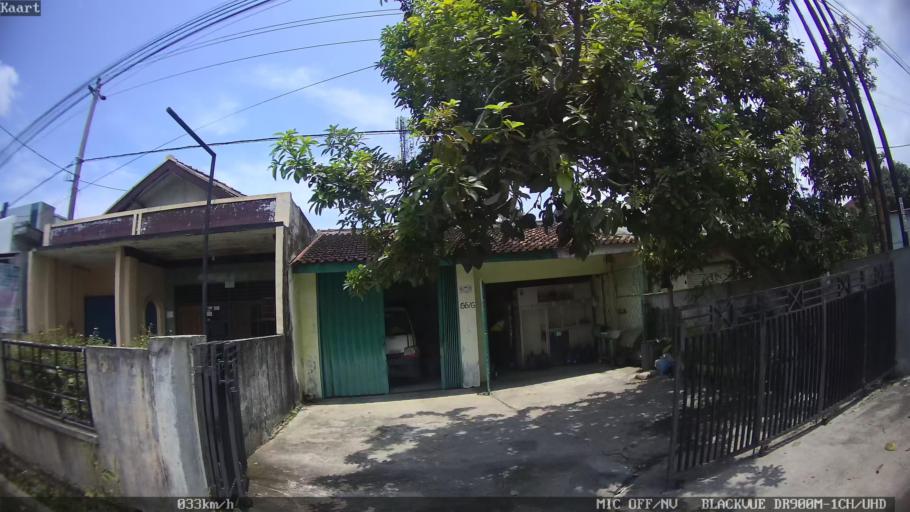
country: ID
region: Lampung
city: Kedaton
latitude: -5.3856
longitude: 105.2552
